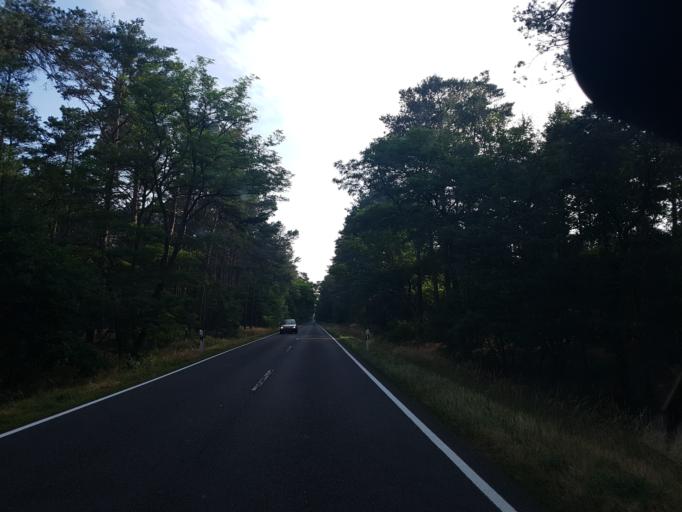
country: DE
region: Brandenburg
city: Schlieben
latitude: 51.7376
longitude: 13.3305
